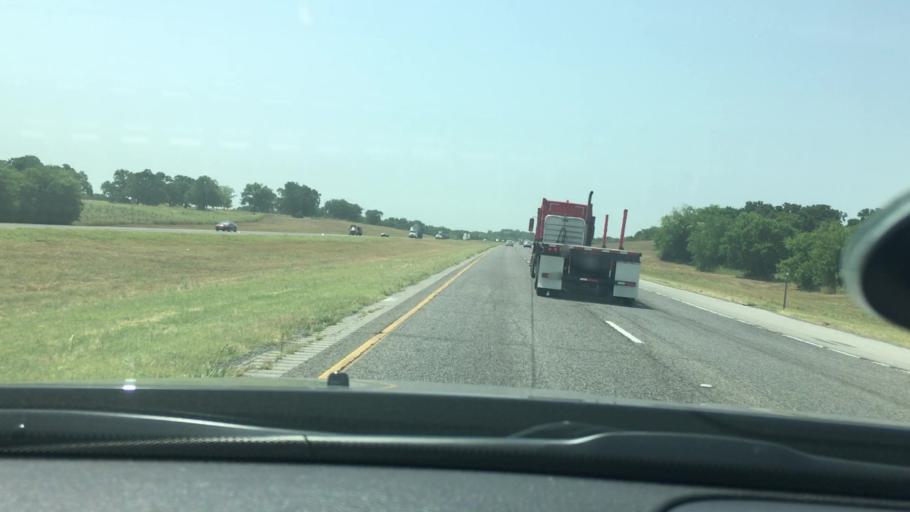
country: US
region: Oklahoma
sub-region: Garvin County
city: Wynnewood
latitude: 34.5911
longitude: -97.2064
